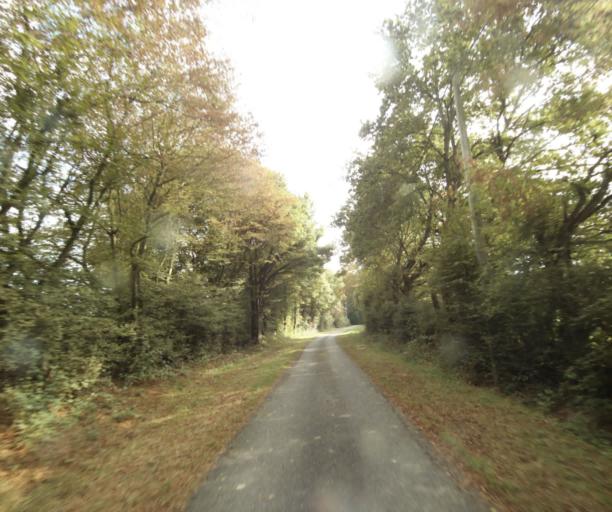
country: FR
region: Bourgogne
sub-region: Departement de Saone-et-Loire
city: Palinges
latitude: 46.5227
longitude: 4.2461
